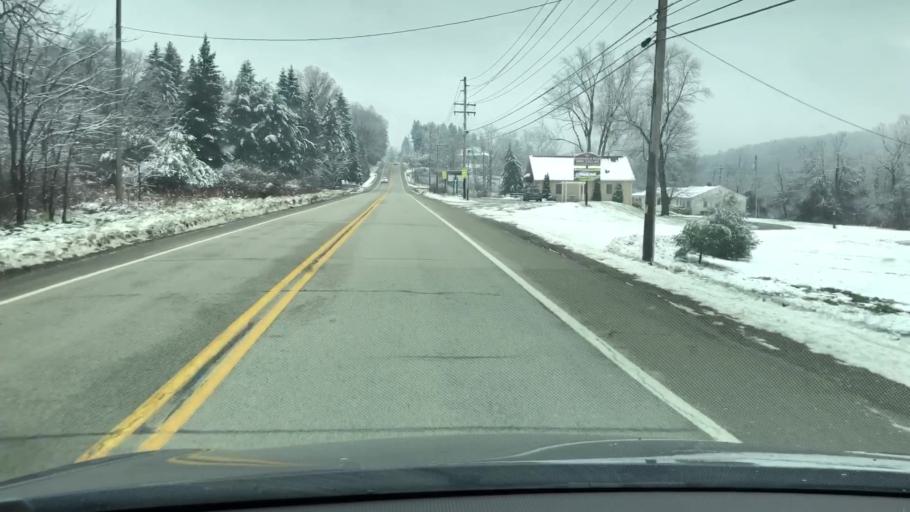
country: US
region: Pennsylvania
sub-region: Fayette County
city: Hopwood
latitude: 39.8238
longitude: -79.5930
